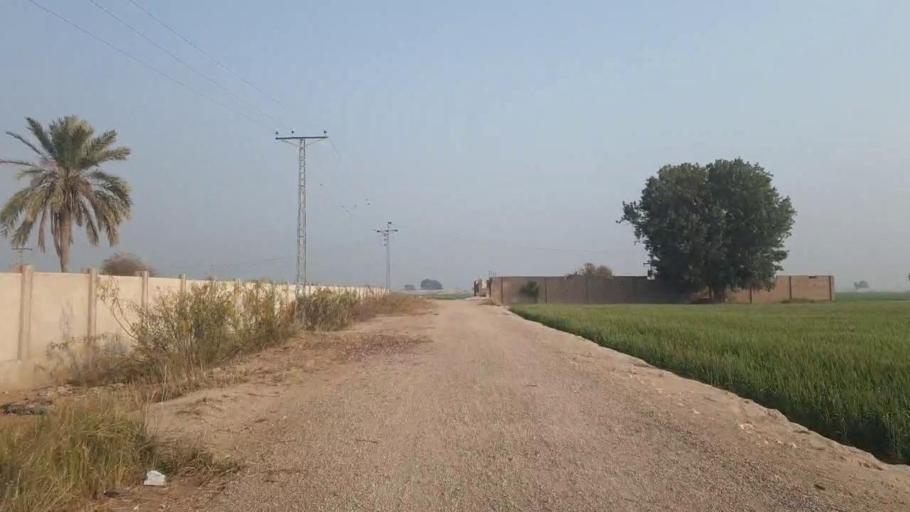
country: PK
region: Sindh
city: Hala
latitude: 25.8045
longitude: 68.4082
